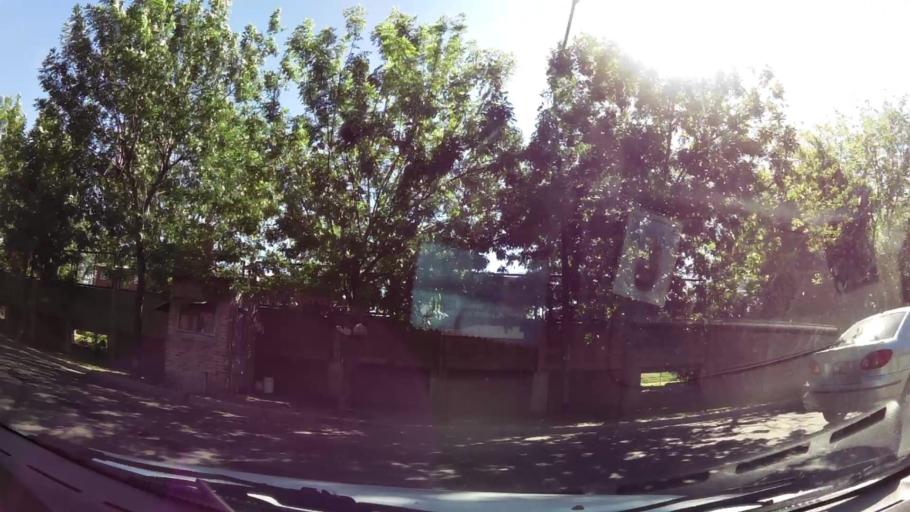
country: AR
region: Buenos Aires
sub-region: Partido de San Isidro
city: San Isidro
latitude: -34.4720
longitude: -58.5318
